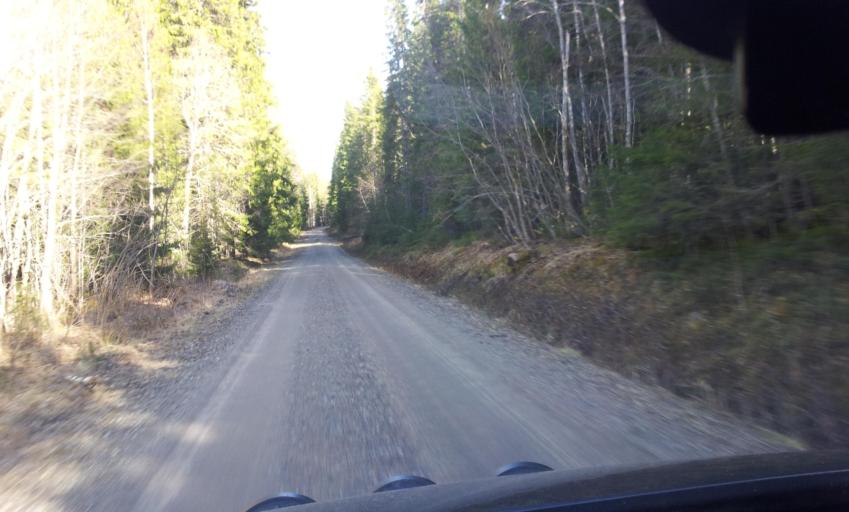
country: SE
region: Vaesternorrland
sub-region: Ange Kommun
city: Ange
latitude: 62.2118
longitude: 15.4163
